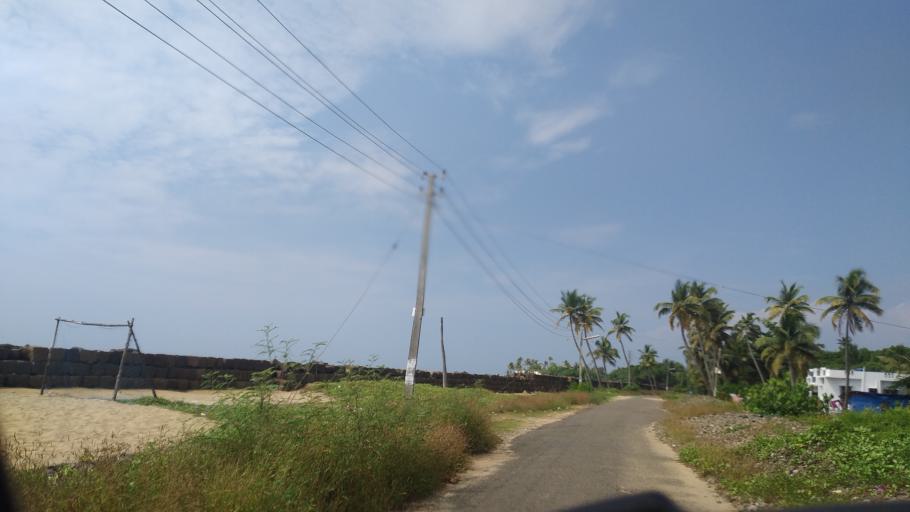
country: IN
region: Kerala
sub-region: Ernakulam
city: Elur
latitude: 10.0487
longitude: 76.2051
